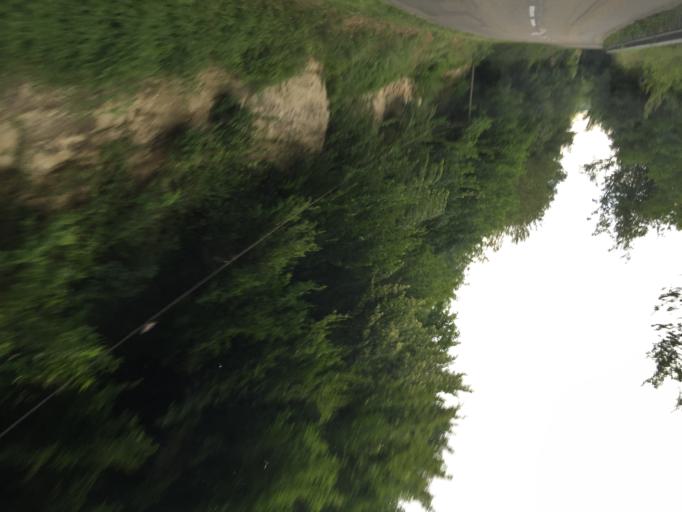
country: FR
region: Rhone-Alpes
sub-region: Departement de la Savoie
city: Le Pont-de-Beauvoisin
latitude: 45.5524
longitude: 5.6754
